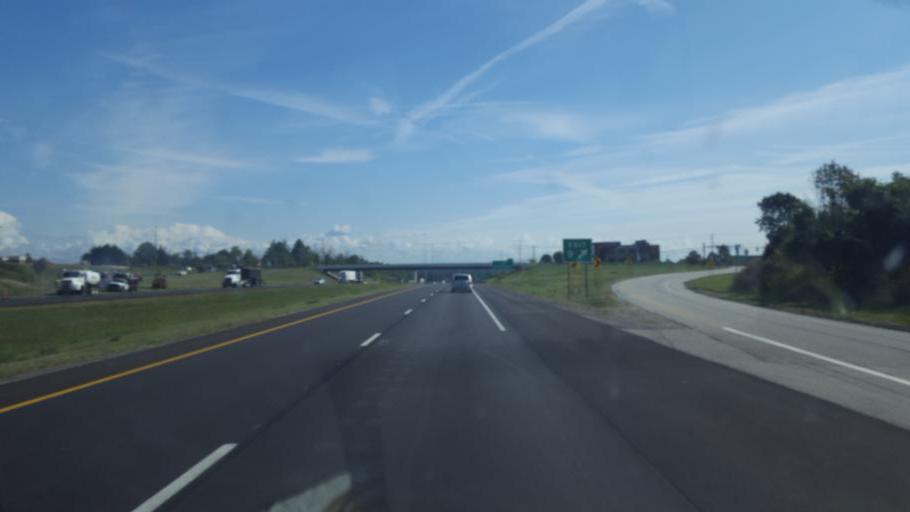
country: US
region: Ohio
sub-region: Summit County
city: Richfield
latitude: 41.2222
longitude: -81.6407
